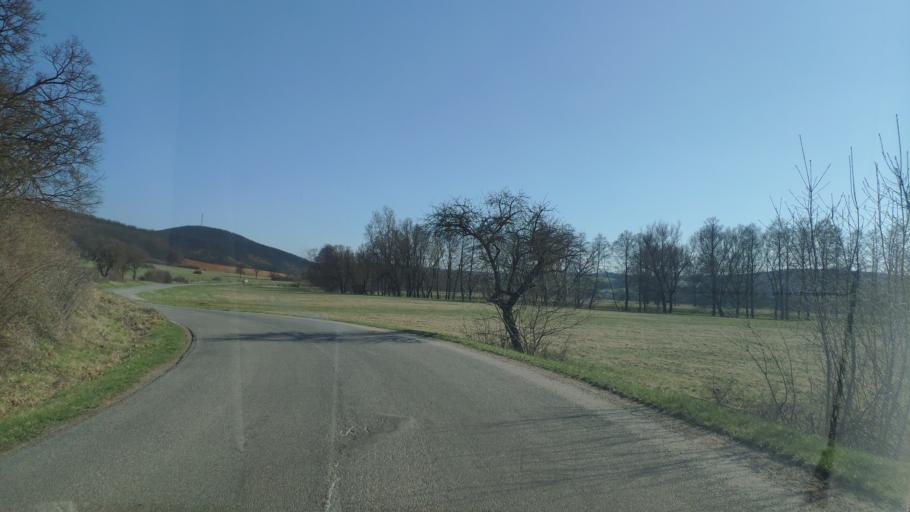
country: SK
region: Banskobystricky
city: Revuca
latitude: 48.5458
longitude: 20.3017
